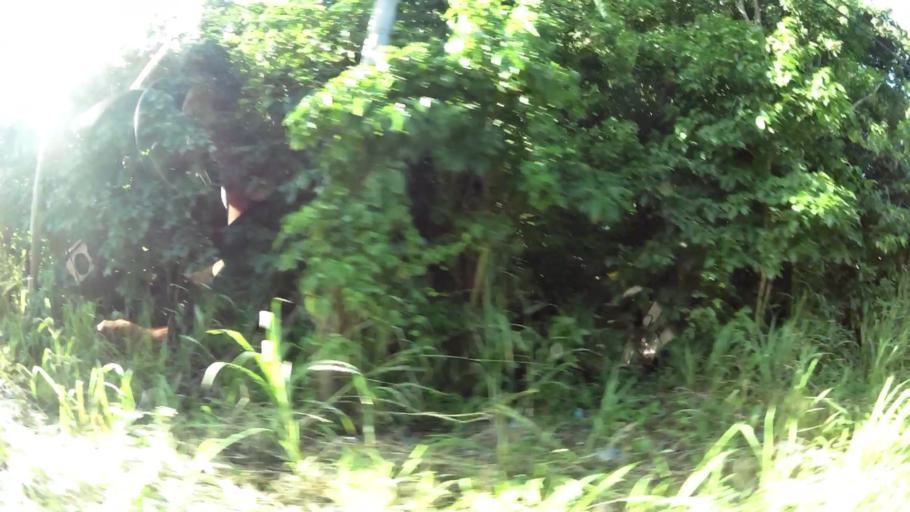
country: GP
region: Guadeloupe
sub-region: Guadeloupe
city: Petit-Canal
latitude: 16.3223
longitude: -61.4380
